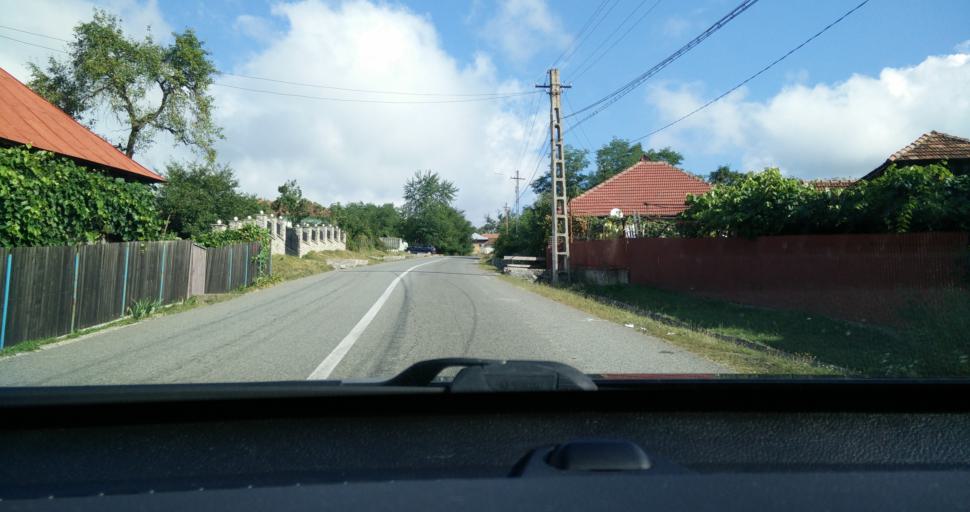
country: RO
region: Gorj
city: Novaci-Straini
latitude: 45.1828
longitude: 23.6819
